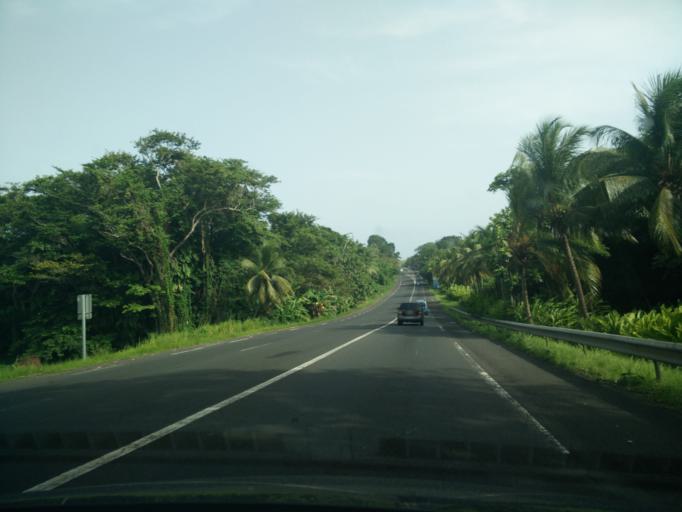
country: GP
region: Guadeloupe
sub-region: Guadeloupe
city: Petit-Bourg
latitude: 16.1386
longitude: -61.5817
